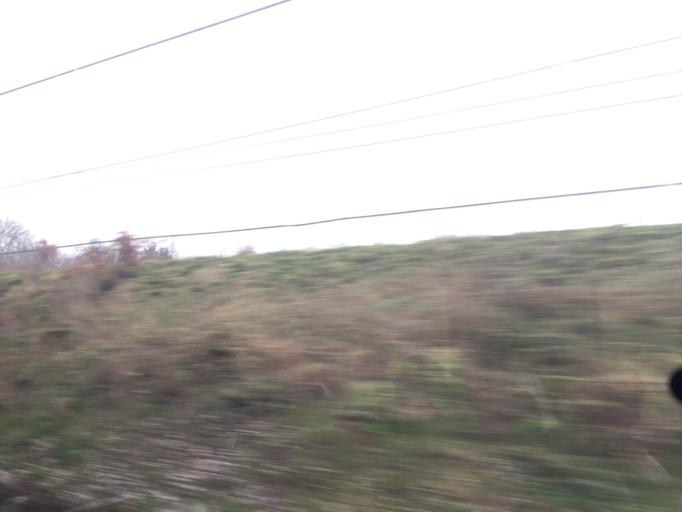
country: GB
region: England
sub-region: Lancashire
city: Leyland
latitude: 53.6865
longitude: -2.6812
